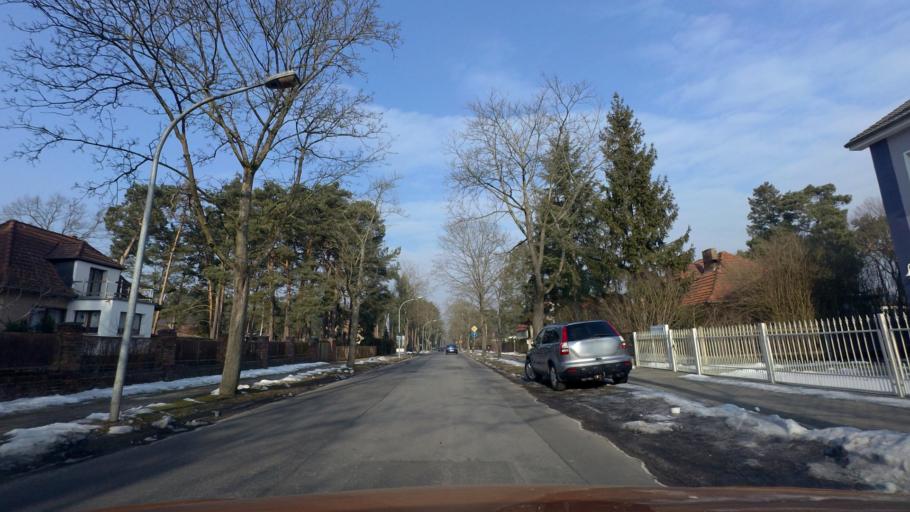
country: DE
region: Brandenburg
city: Am Mellensee
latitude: 52.1720
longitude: 13.4014
